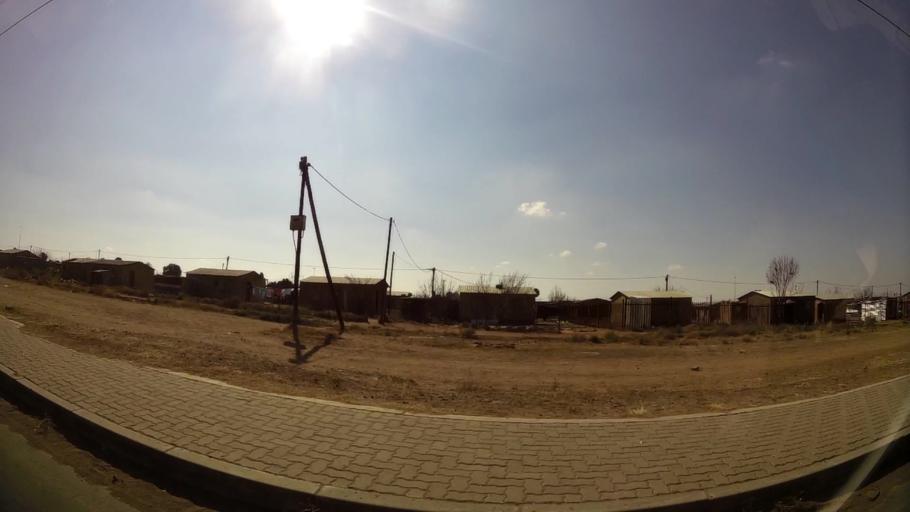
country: ZA
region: Orange Free State
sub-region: Mangaung Metropolitan Municipality
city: Bloemfontein
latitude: -29.1660
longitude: 26.2849
